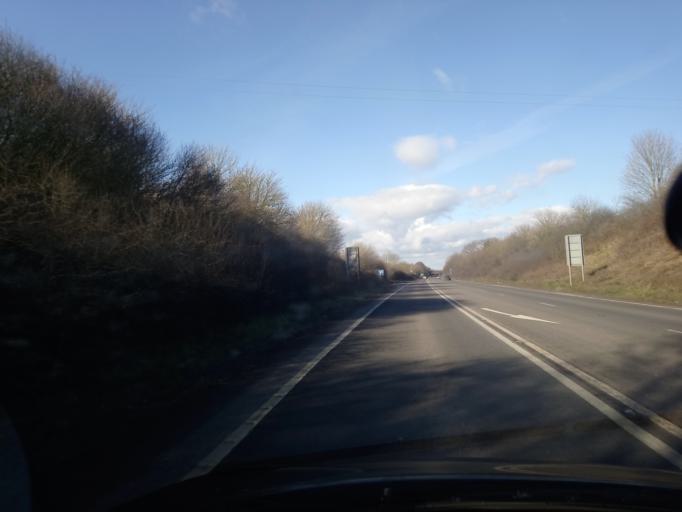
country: GB
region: England
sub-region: Shropshire
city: Whitchurch
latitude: 52.9587
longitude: -2.6962
